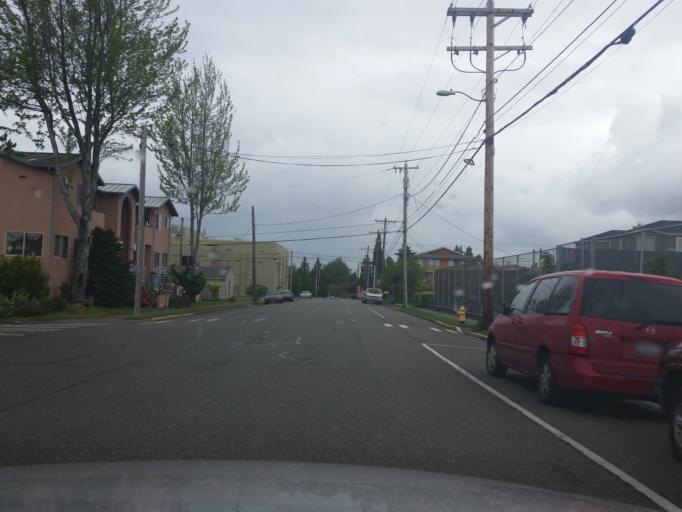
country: US
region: Washington
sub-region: Snohomish County
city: Edmonds
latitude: 47.8127
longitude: -122.3749
